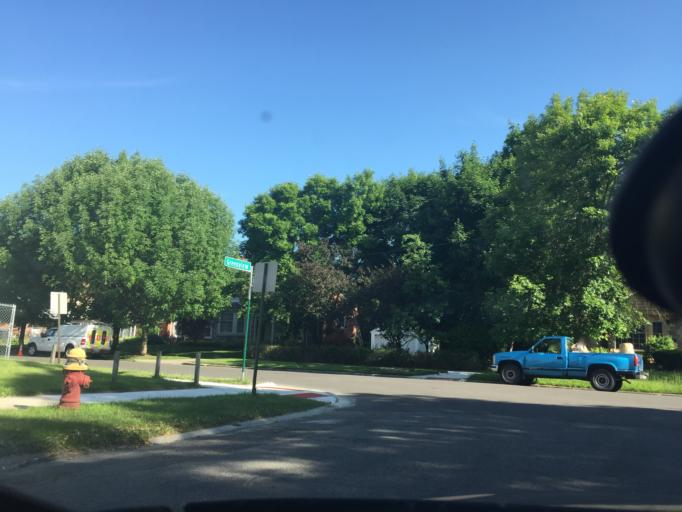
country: US
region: Michigan
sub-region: Oakland County
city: Southfield
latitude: 42.4084
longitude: -83.2239
